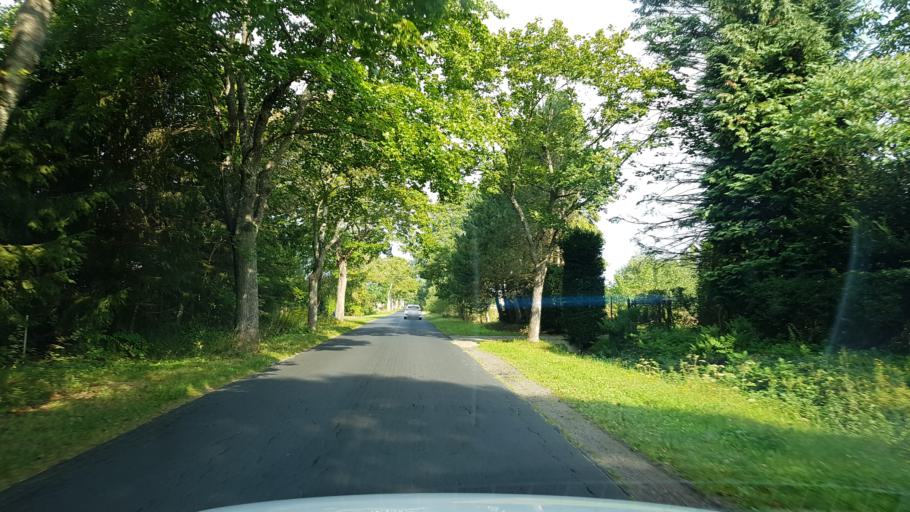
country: PL
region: West Pomeranian Voivodeship
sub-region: Powiat slawienski
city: Slawno
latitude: 54.4503
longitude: 16.5970
